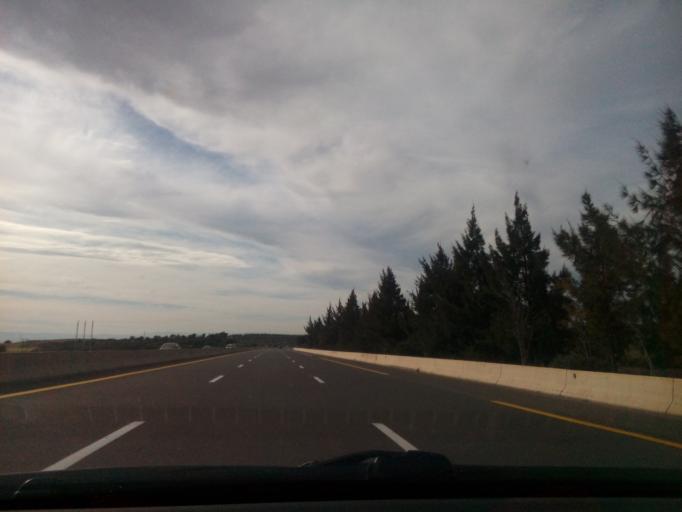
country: DZ
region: Sidi Bel Abbes
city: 'Ain el Berd
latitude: 35.3443
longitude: -0.5163
